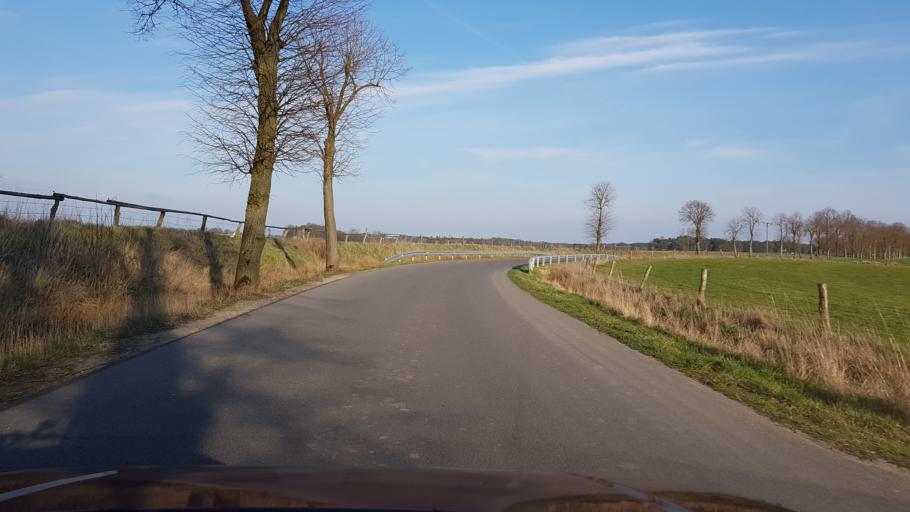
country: PL
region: West Pomeranian Voivodeship
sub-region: Powiat bialogardzki
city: Bialogard
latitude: 54.1243
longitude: 15.9977
